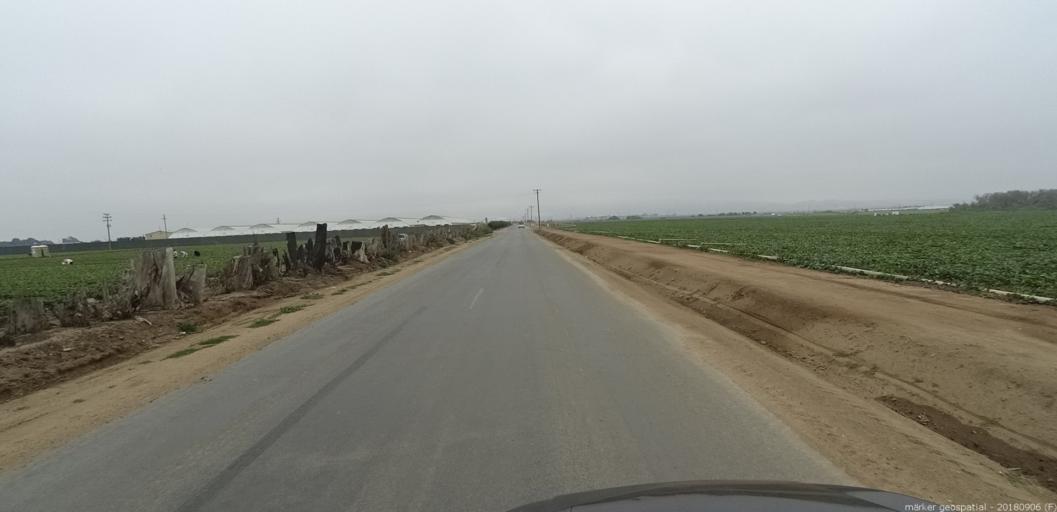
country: US
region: California
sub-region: Monterey County
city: Chualar
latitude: 36.6481
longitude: -121.5646
